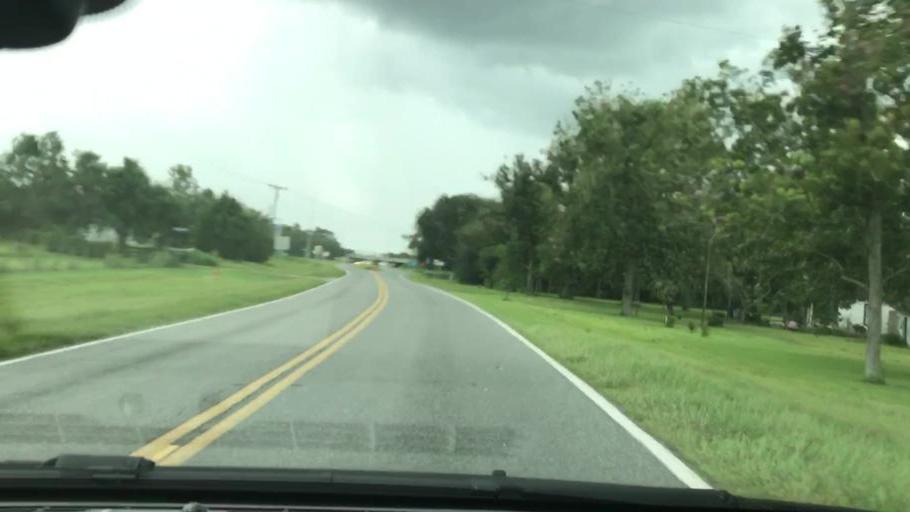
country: US
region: Florida
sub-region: Madison County
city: Madison
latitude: 30.3848
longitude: -83.3002
